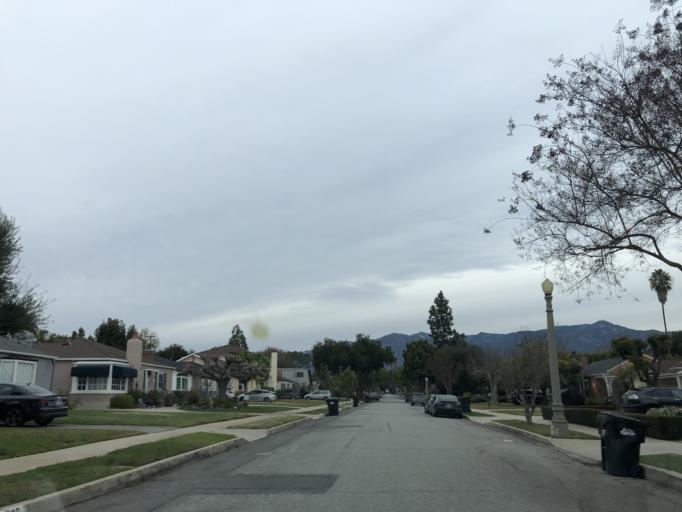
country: US
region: California
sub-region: Los Angeles County
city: San Marino
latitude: 34.1102
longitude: -118.1061
